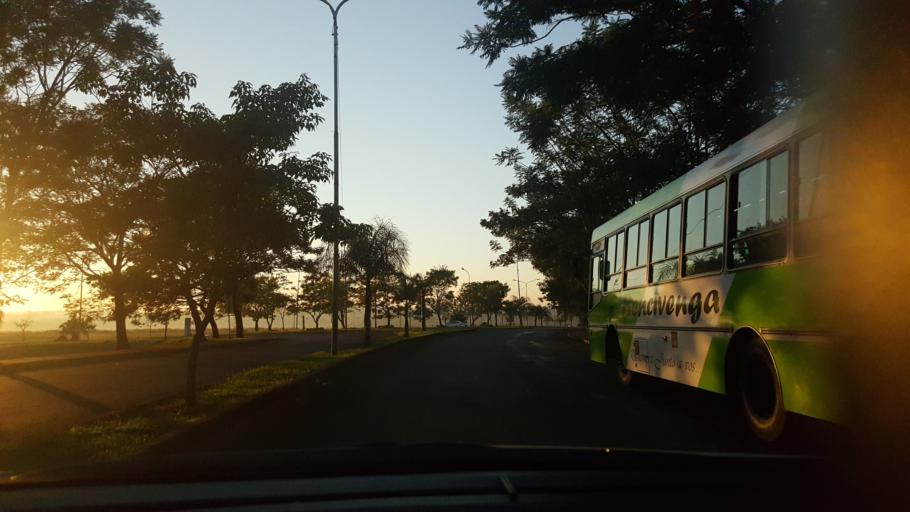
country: AR
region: Misiones
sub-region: Departamento de Capital
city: Posadas
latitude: -27.3924
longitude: -55.9642
